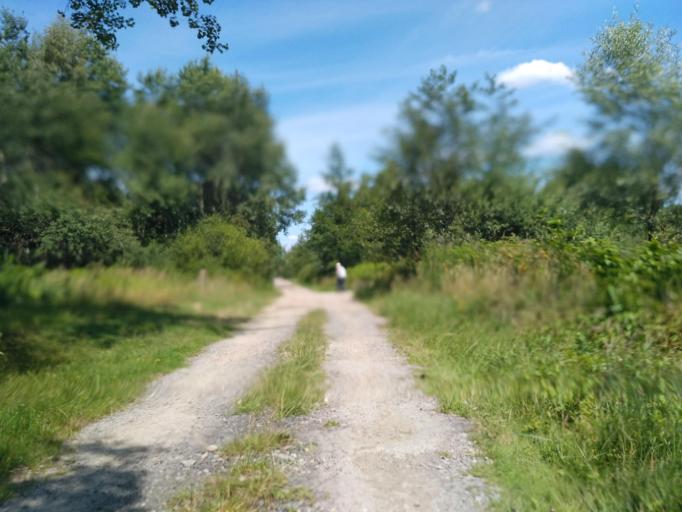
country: PL
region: Subcarpathian Voivodeship
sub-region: Powiat krosnienski
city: Kroscienko Wyzne
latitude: 49.6471
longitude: 21.8507
